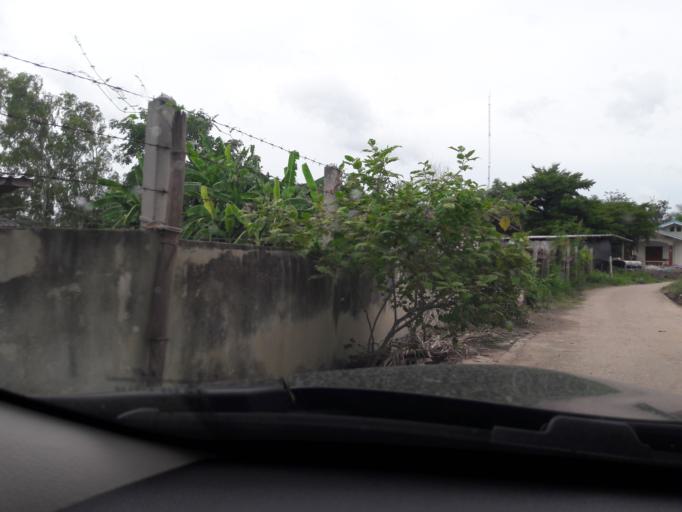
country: TH
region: Ratchaburi
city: Damnoen Saduak
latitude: 13.5982
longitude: 99.9051
